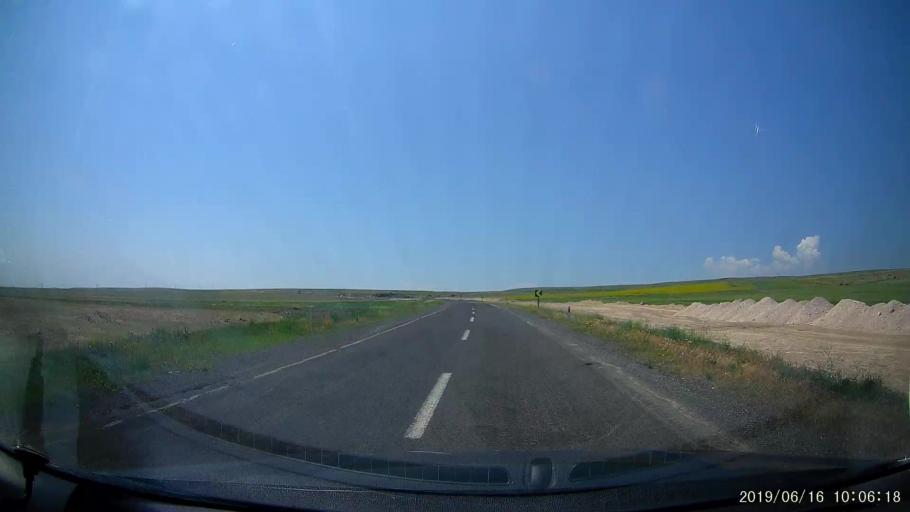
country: TR
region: Kars
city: Digor
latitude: 40.2573
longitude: 43.5416
